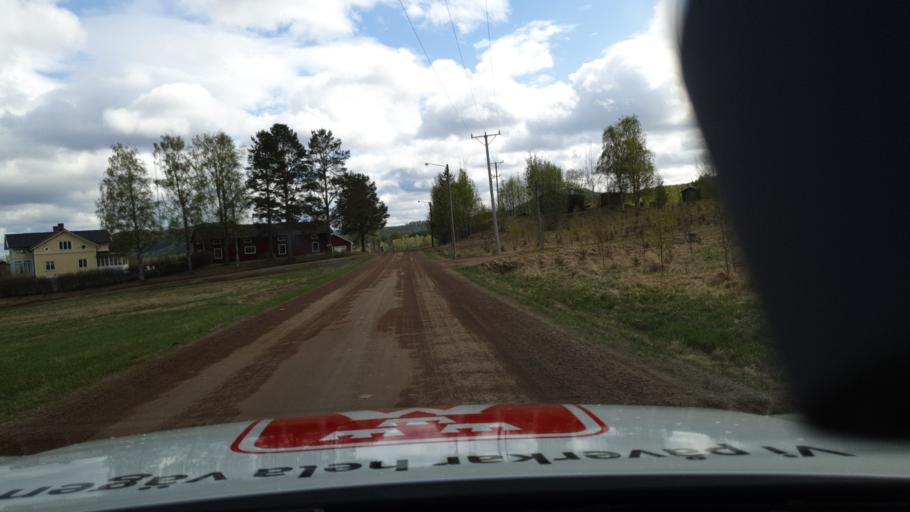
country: SE
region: Jaemtland
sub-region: Ragunda Kommun
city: Hammarstrand
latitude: 63.0980
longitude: 16.3280
